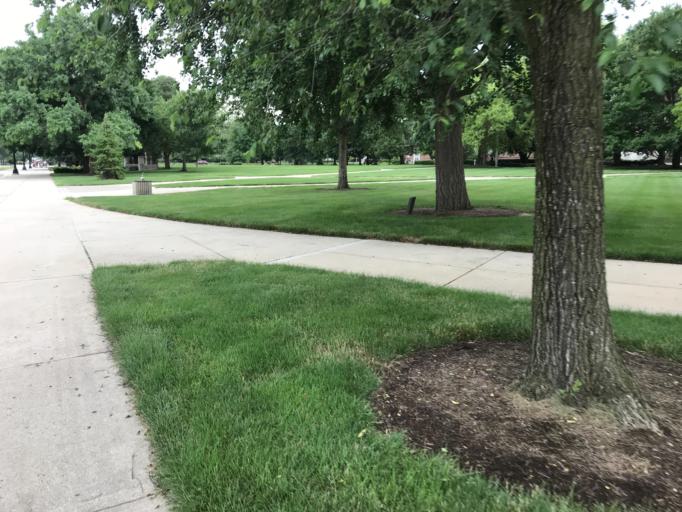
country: US
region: Indiana
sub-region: Tippecanoe County
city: West Lafayette
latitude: 40.4261
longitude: -86.9139
